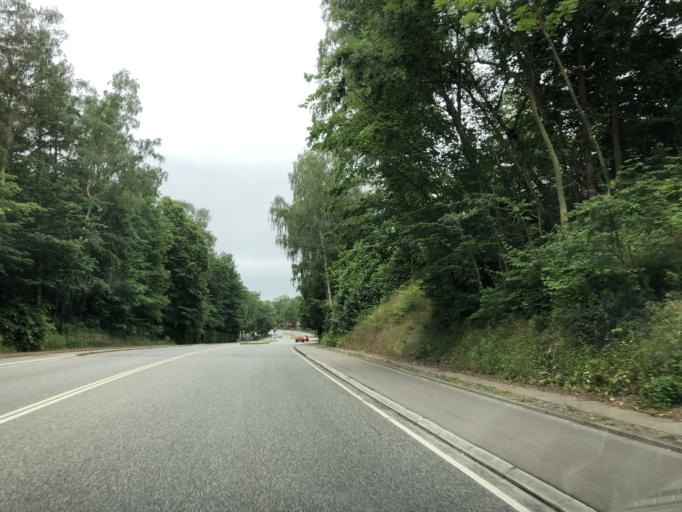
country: DK
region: Capital Region
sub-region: Lyngby-Tarbaek Kommune
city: Kongens Lyngby
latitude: 55.8110
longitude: 12.5120
